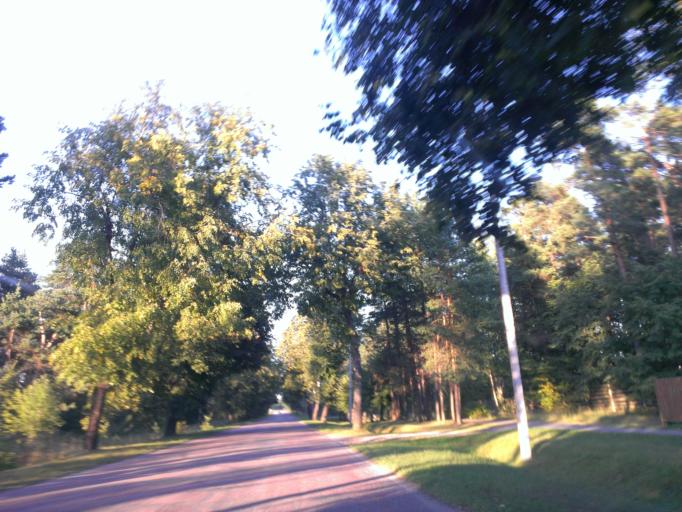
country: LV
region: Garkalne
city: Garkalne
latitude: 57.0492
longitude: 24.4295
